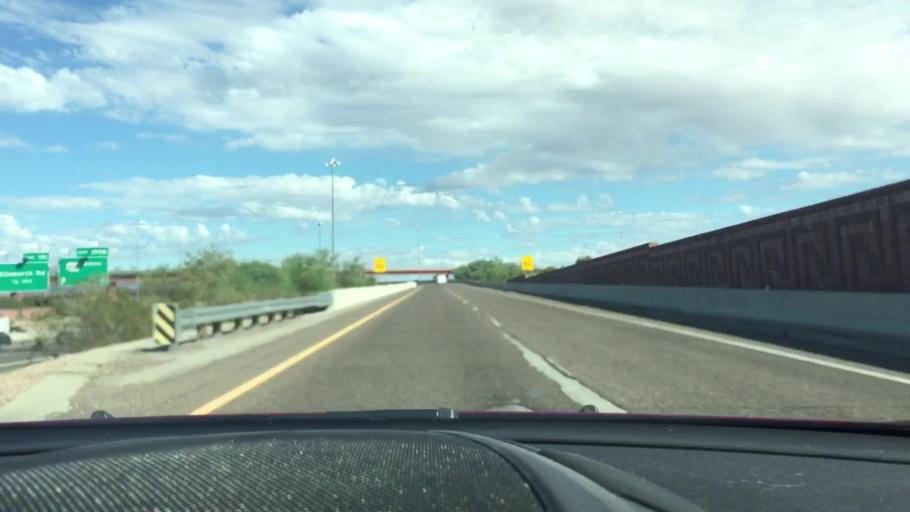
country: US
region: Arizona
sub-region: Pinal County
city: Apache Junction
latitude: 33.3862
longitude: -111.6545
